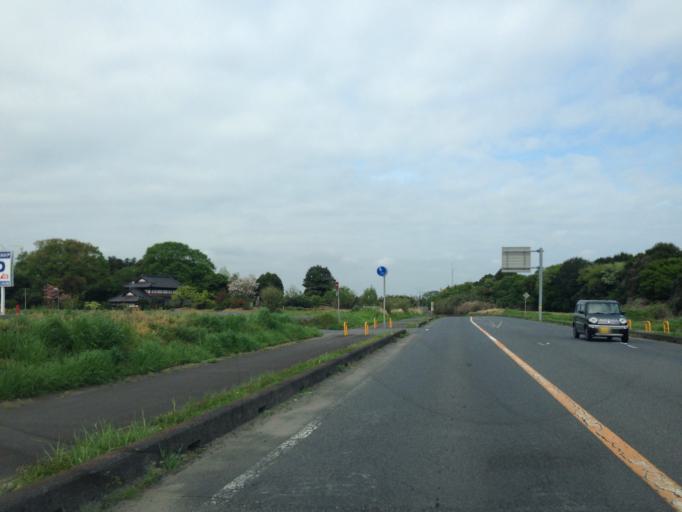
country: JP
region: Ibaraki
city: Ishige
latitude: 36.1487
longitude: 140.0149
